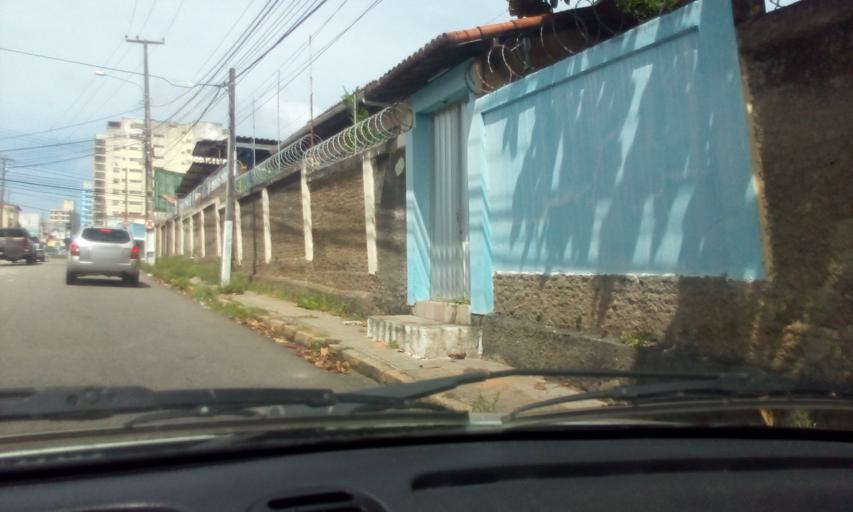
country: BR
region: Rio Grande do Norte
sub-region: Natal
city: Natal
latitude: -5.7912
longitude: -35.2062
